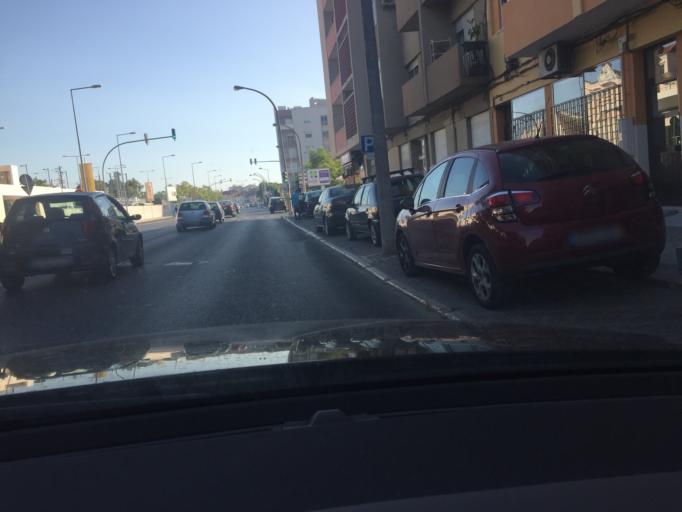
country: PT
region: Setubal
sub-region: Setubal
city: Setubal
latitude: 38.5315
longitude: -8.8852
